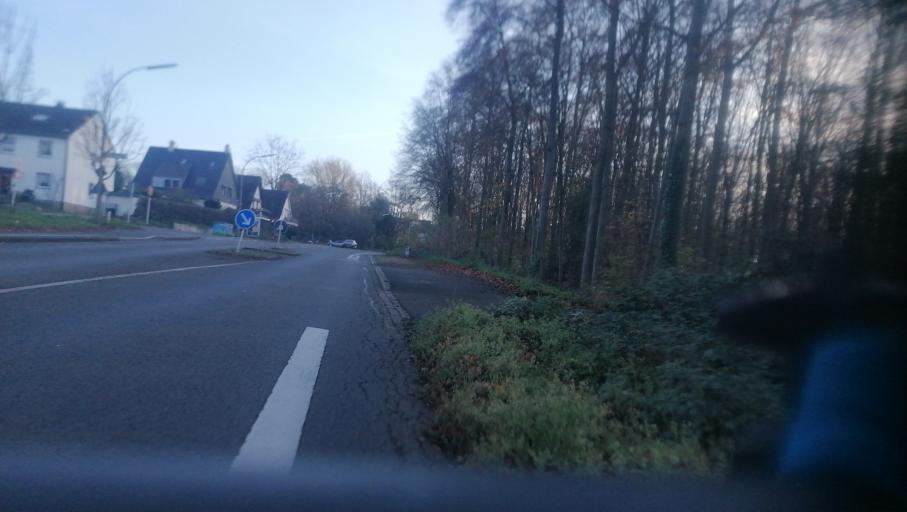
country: DE
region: North Rhine-Westphalia
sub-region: Regierungsbezirk Arnsberg
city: Dortmund
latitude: 51.4507
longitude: 7.4879
